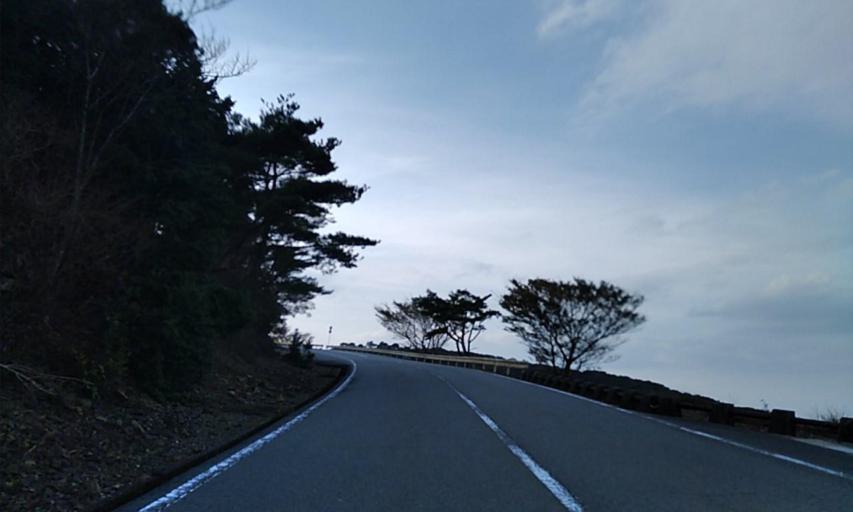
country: JP
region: Mie
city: Toba
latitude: 34.4601
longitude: 136.7964
